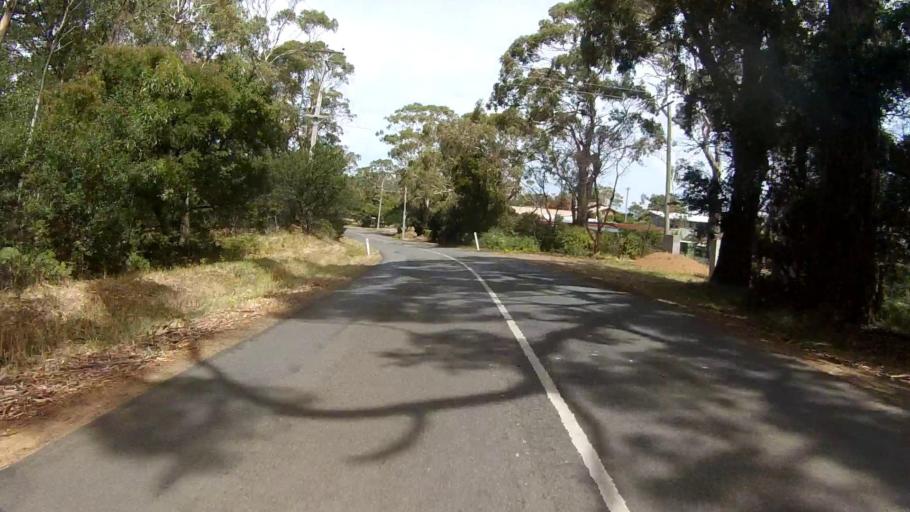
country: AU
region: Tasmania
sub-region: Kingborough
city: Taroona
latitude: -43.0204
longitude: 147.4180
